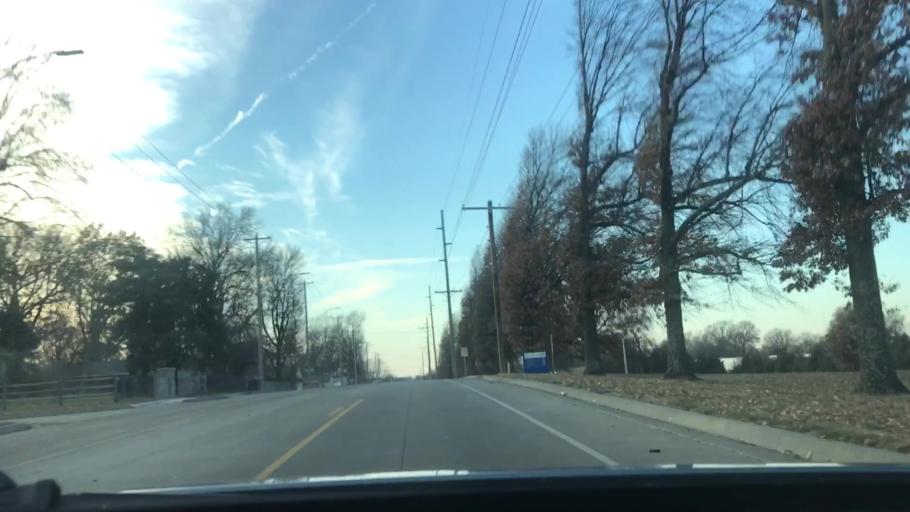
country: US
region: Missouri
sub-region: Jackson County
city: Independence
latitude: 39.0576
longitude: -94.4202
